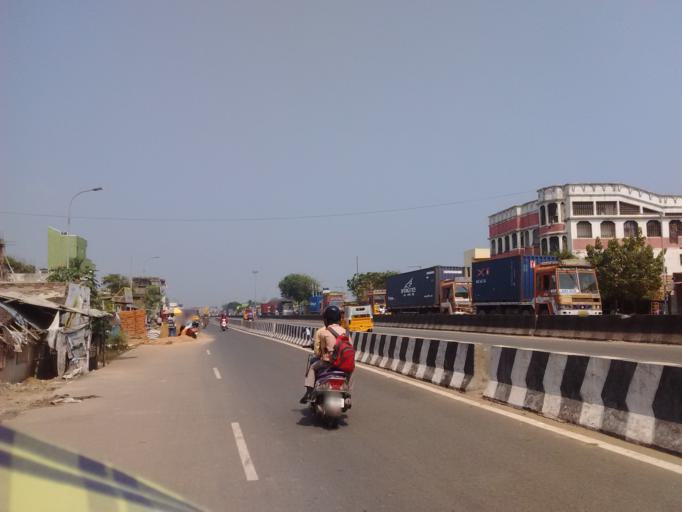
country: IN
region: Tamil Nadu
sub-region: Thiruvallur
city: Tiruvottiyur
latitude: 13.1591
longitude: 80.3057
